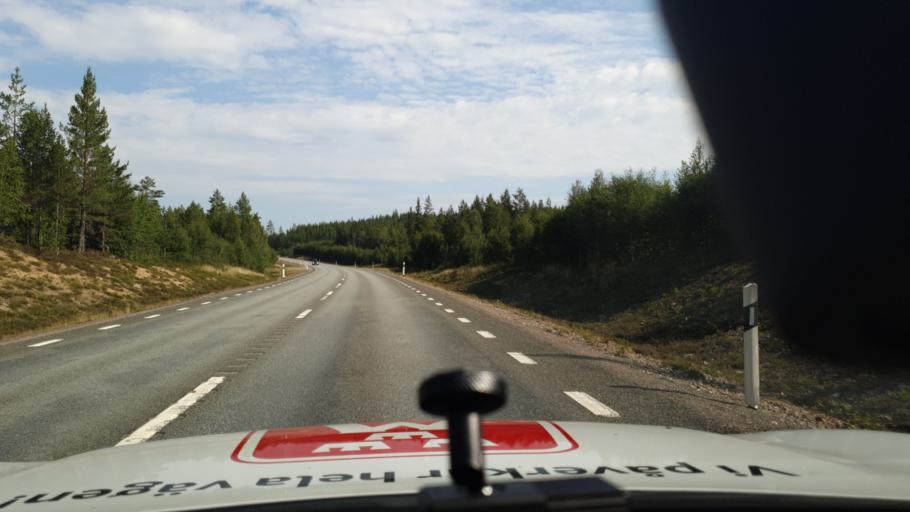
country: SE
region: Vaermland
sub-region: Hagfors Kommun
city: Ekshaerad
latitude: 60.5022
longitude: 13.4263
